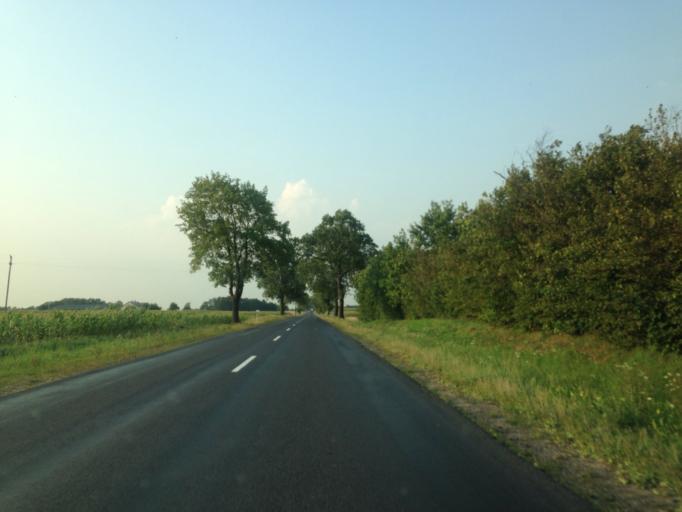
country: PL
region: Kujawsko-Pomorskie
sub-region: Powiat lipnowski
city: Chrostkowo
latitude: 52.9106
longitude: 19.2393
